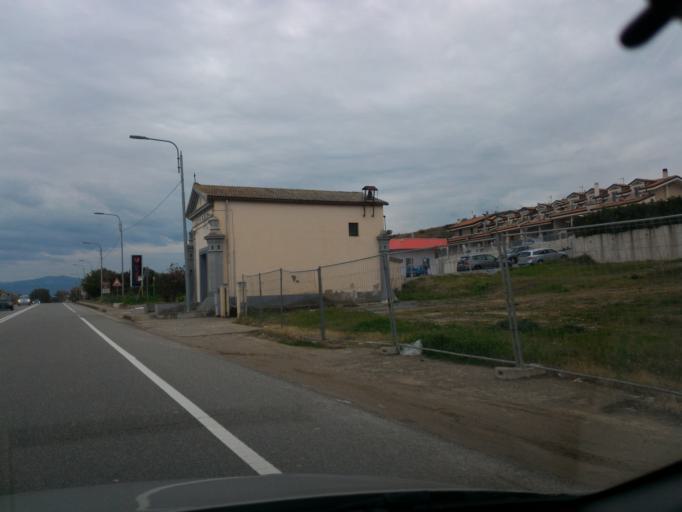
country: IT
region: Calabria
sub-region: Provincia di Catanzaro
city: Barone
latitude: 38.8382
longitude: 16.6405
